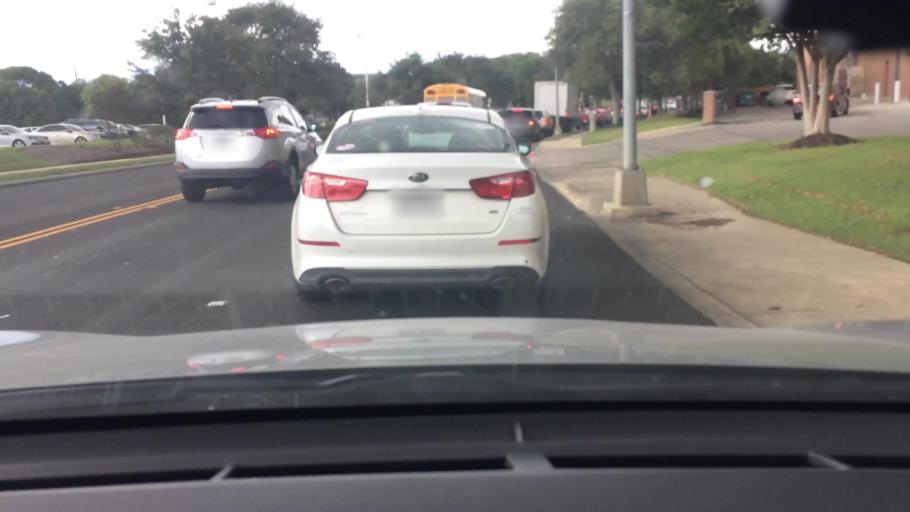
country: US
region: Texas
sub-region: Bexar County
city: Shavano Park
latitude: 29.5614
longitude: -98.5934
